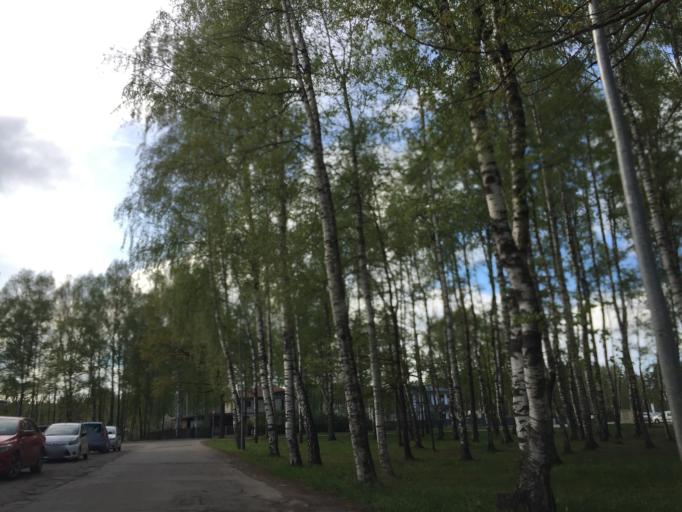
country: LV
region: Kekava
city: Balozi
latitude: 56.8810
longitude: 24.1500
